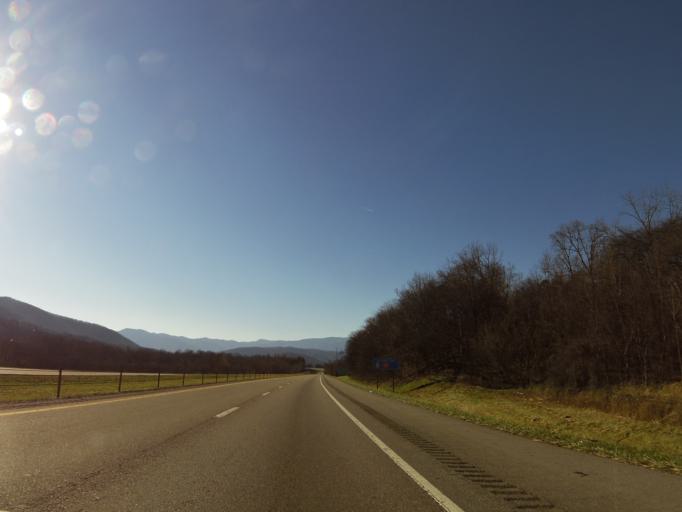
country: US
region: Tennessee
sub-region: Cocke County
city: Newport
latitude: 35.8988
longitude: -83.1842
